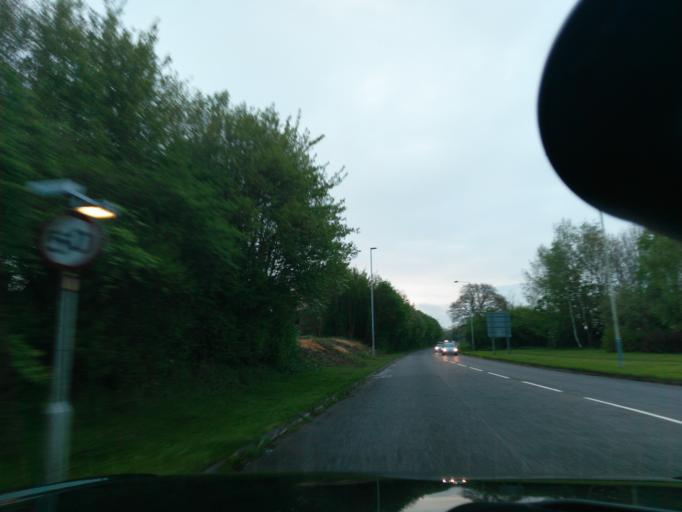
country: GB
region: England
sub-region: Wiltshire
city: Trowbridge
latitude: 51.3265
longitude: -2.1776
